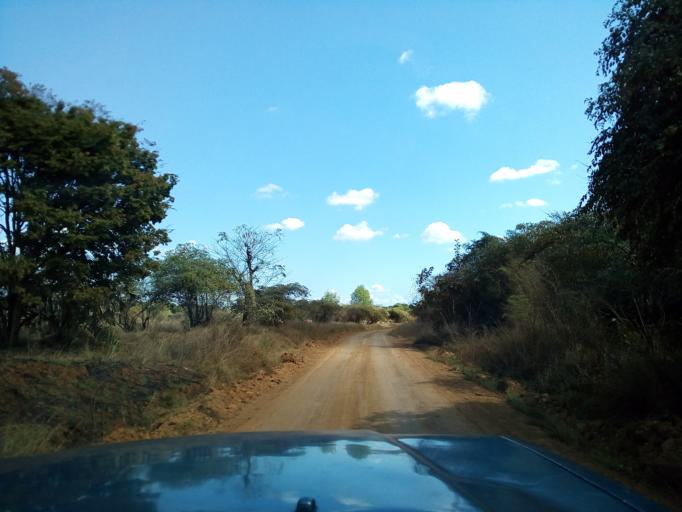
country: MG
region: Boeny
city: Mahajanga
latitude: -16.0008
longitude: 46.0455
